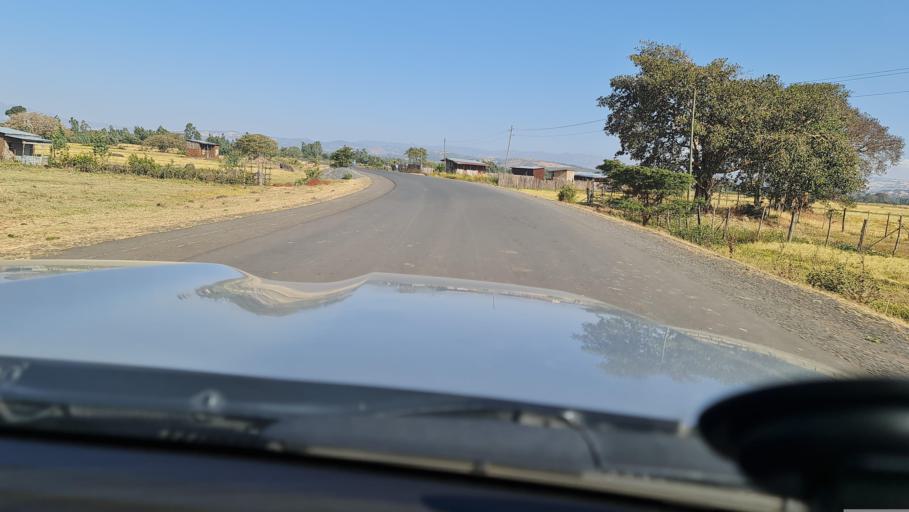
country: ET
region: Oromiya
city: Waliso
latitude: 8.5580
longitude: 37.9490
